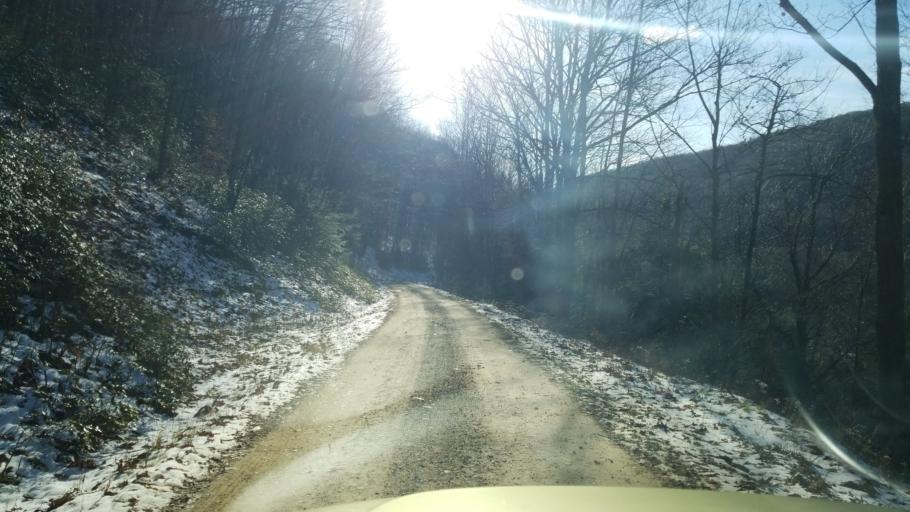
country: US
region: Pennsylvania
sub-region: Jefferson County
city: Brockway
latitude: 41.2966
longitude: -78.8292
